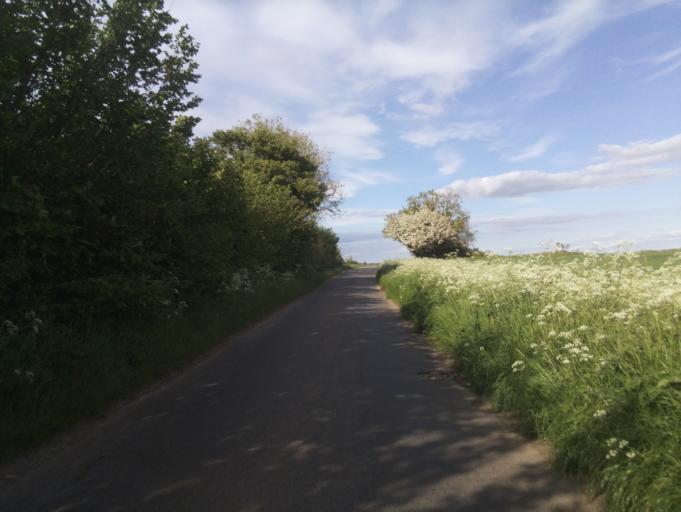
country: GB
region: England
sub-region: Gloucestershire
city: Donnington
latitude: 51.9482
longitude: -1.7824
